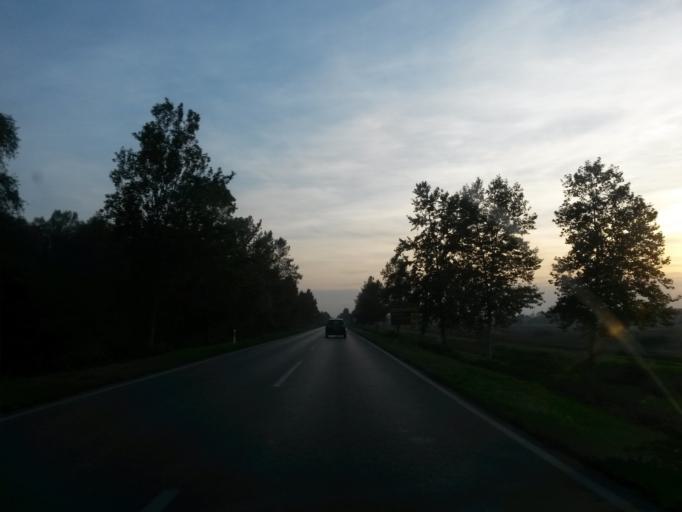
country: HR
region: Osjecko-Baranjska
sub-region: Grad Osijek
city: Osijek
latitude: 45.5779
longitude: 18.7198
